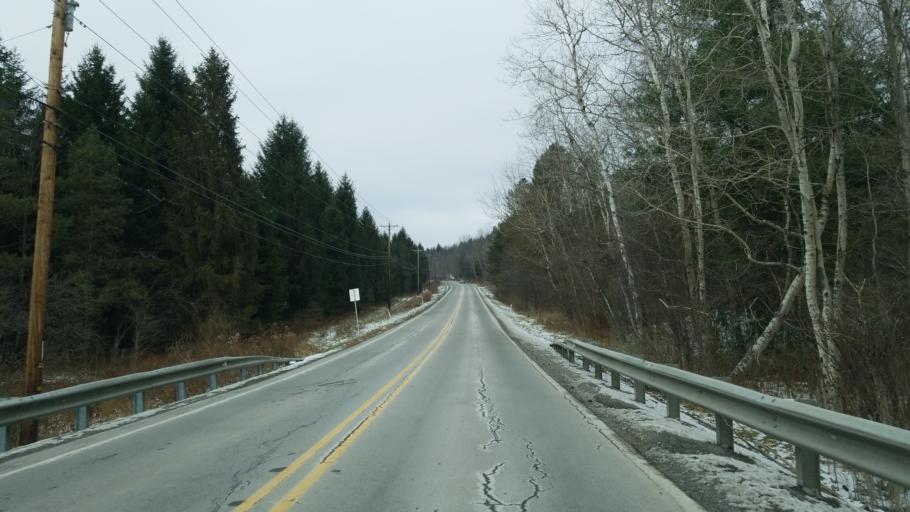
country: US
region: Pennsylvania
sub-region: Clearfield County
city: Sandy
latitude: 41.0780
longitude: -78.7350
